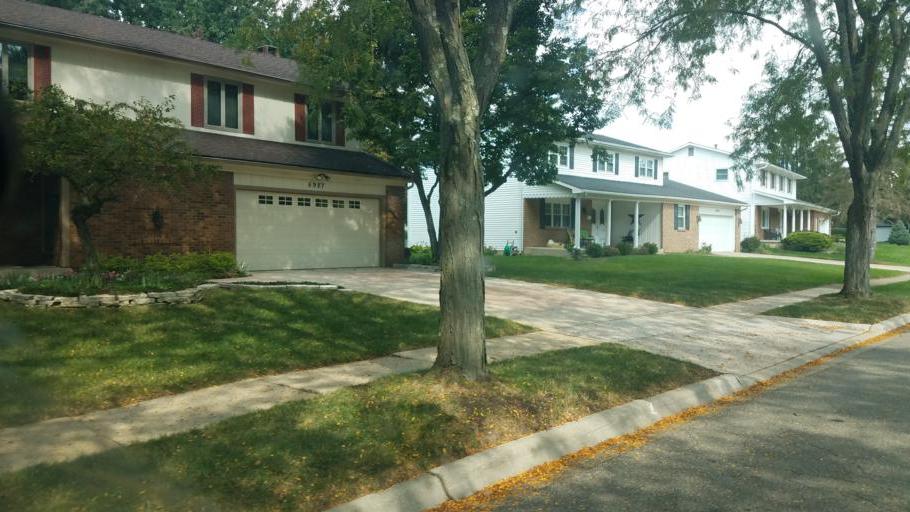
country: US
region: Ohio
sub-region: Franklin County
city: Worthington
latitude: 40.1073
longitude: -83.0261
